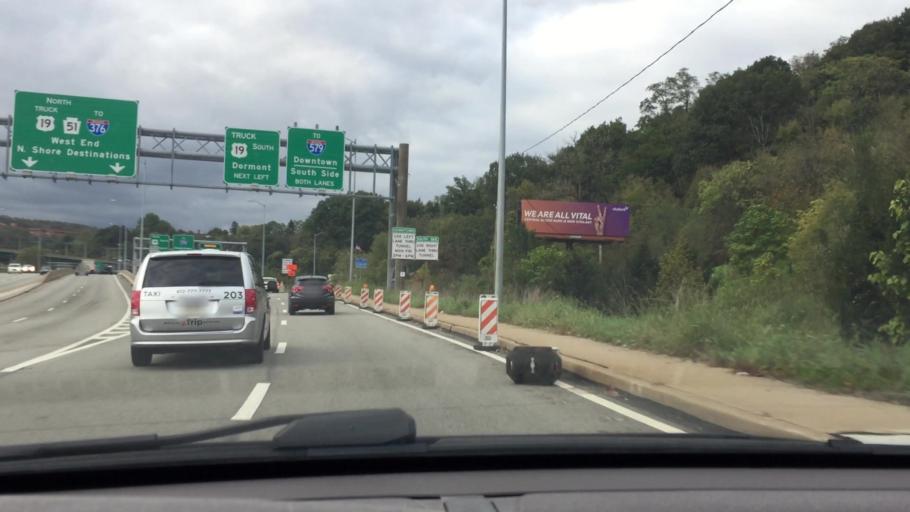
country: US
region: Pennsylvania
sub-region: Allegheny County
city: Mount Oliver
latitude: 40.4127
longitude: -80.0074
